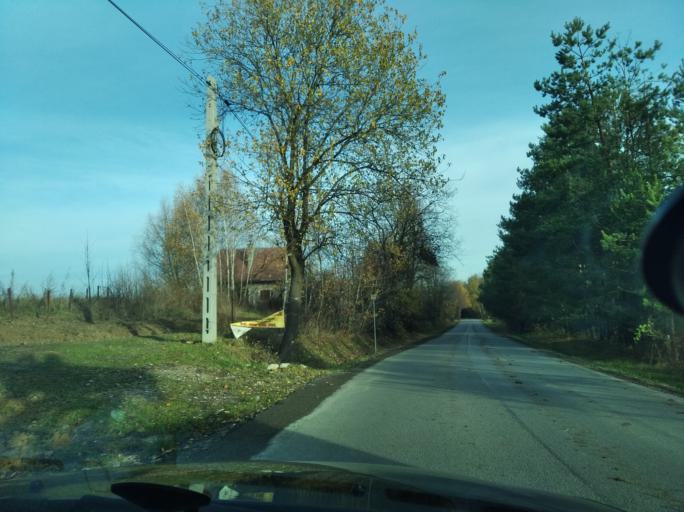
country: PL
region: Subcarpathian Voivodeship
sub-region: Powiat rzeszowski
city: Siedliska
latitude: 49.9422
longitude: 21.9780
